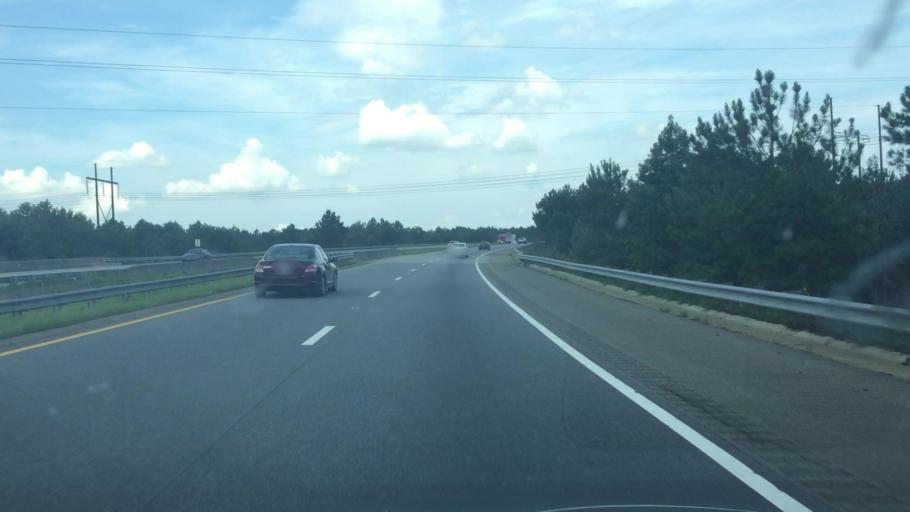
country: US
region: North Carolina
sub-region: Richmond County
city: Hamlet
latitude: 34.8526
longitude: -79.7328
